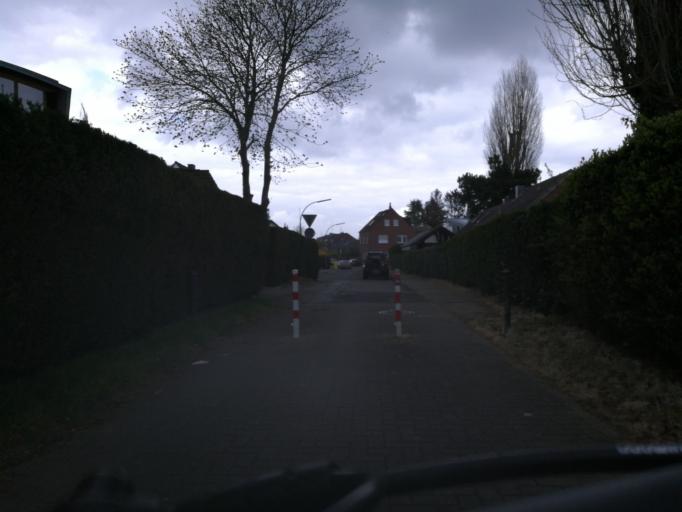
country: DE
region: North Rhine-Westphalia
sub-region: Regierungsbezirk Dusseldorf
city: Dusseldorf
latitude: 51.1594
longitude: 6.7909
